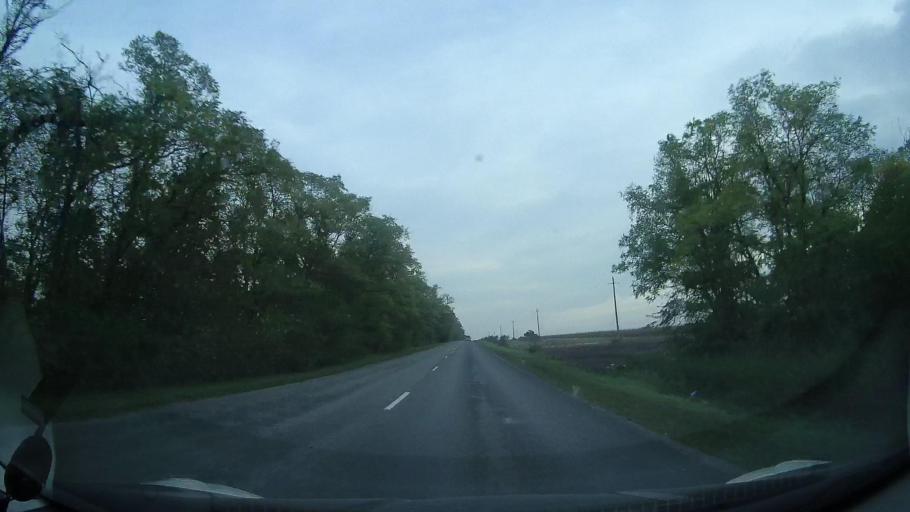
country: RU
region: Rostov
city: Ol'ginskaya
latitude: 47.0993
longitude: 39.9776
